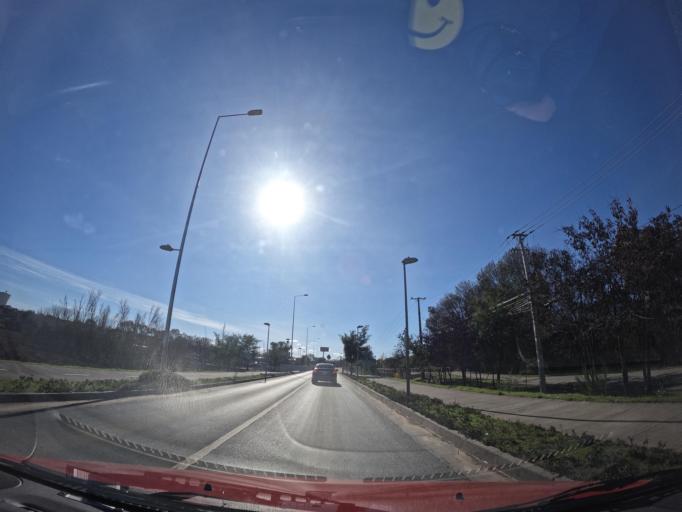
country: CL
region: Maule
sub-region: Provincia de Cauquenes
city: Cauquenes
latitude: -35.9750
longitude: -72.3153
